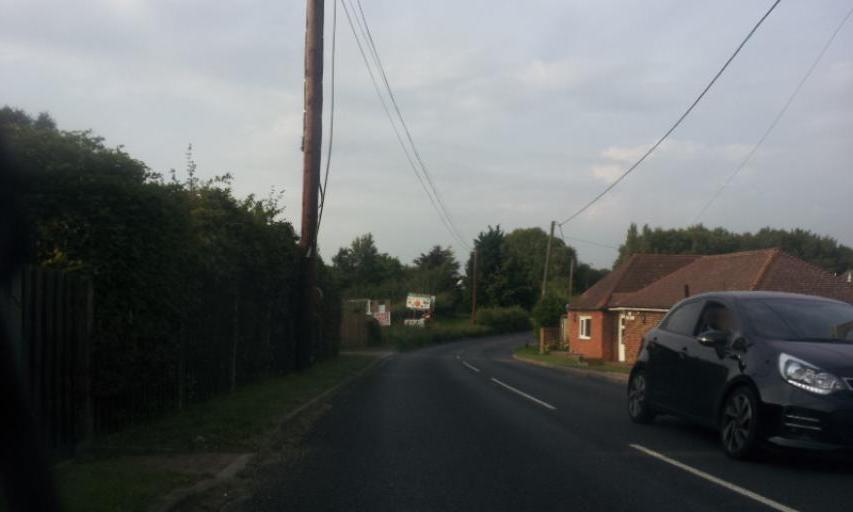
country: GB
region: England
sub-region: Kent
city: Wateringbury
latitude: 51.2683
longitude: 0.4296
